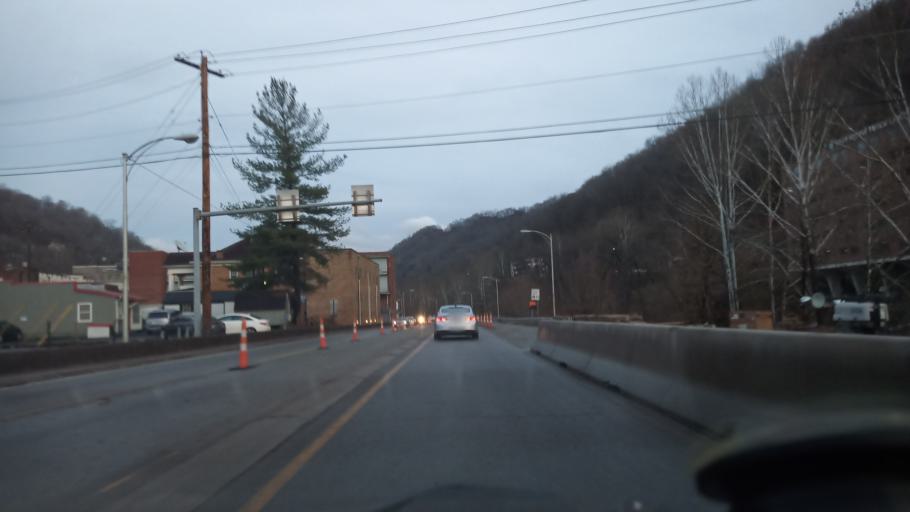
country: US
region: West Virginia
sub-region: Logan County
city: Logan
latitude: 37.8472
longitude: -81.9940
